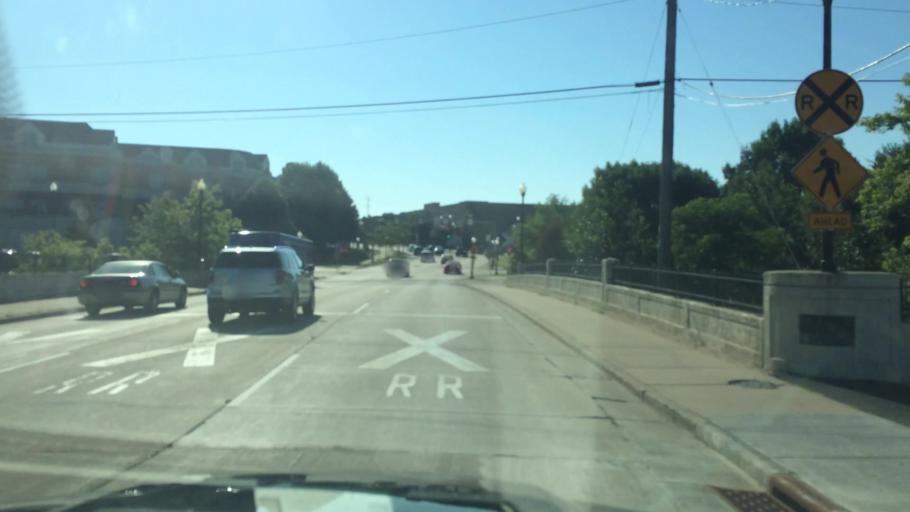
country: US
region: Wisconsin
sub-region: Marathon County
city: Wausau
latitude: 44.9597
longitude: -89.6327
